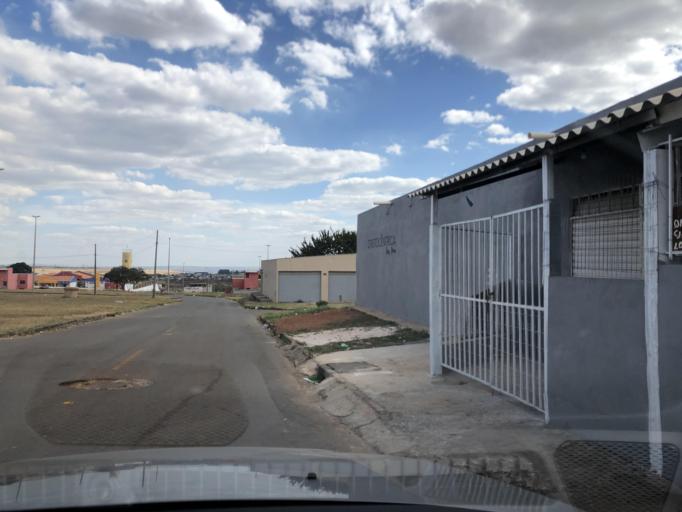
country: BR
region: Federal District
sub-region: Brasilia
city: Brasilia
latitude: -15.8825
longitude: -48.1254
